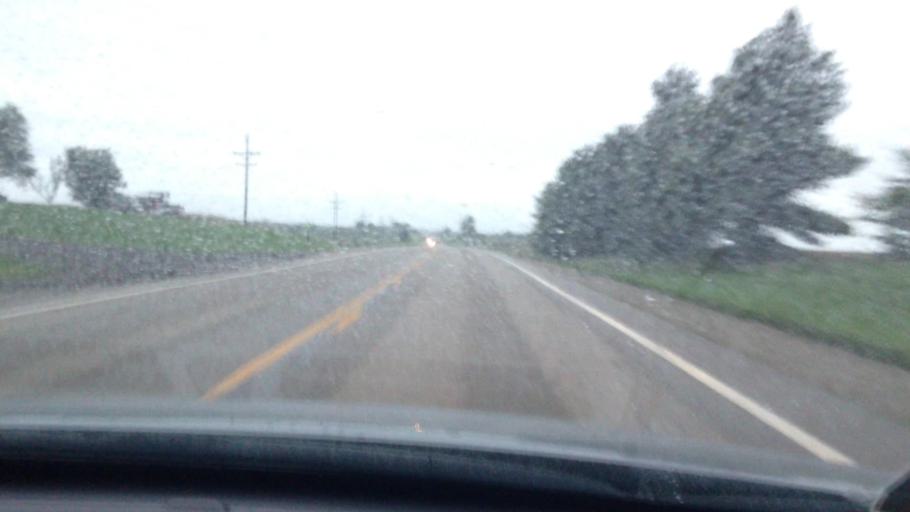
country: US
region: Kansas
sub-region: Brown County
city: Hiawatha
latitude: 39.8163
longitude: -95.5272
